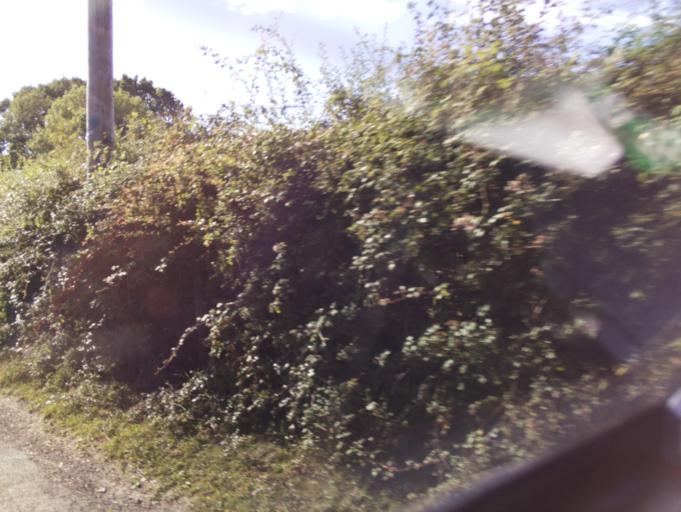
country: GB
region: England
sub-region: Hampshire
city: Cadnam
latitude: 50.9379
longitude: -1.6182
